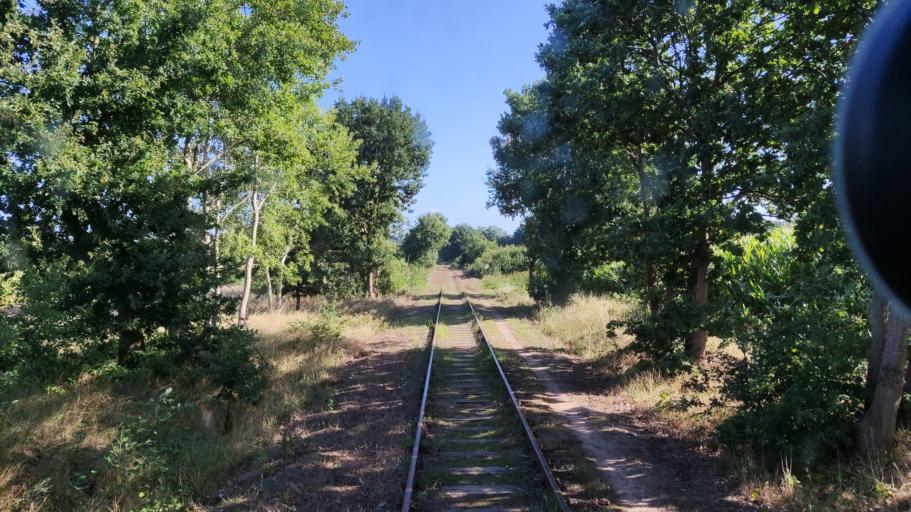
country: DE
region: Lower Saxony
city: Adendorf
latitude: 53.2647
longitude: 10.4662
